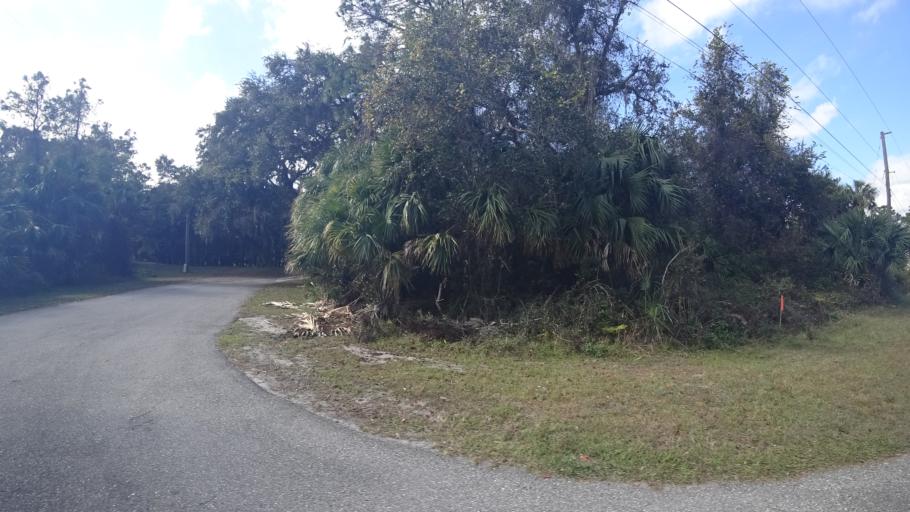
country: US
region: Florida
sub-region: Charlotte County
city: Port Charlotte
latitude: 27.0487
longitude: -82.1282
